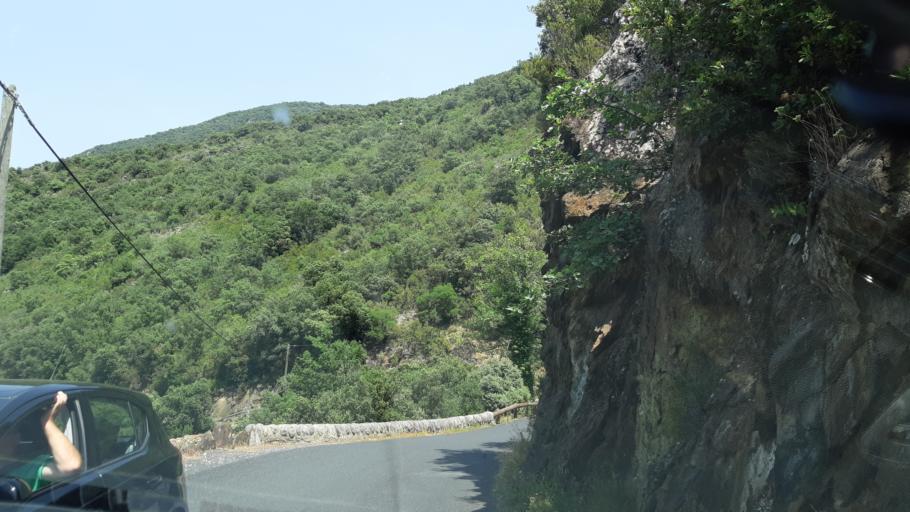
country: FR
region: Languedoc-Roussillon
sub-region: Departement des Pyrenees-Orientales
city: Vinca
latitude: 42.5935
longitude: 2.5117
